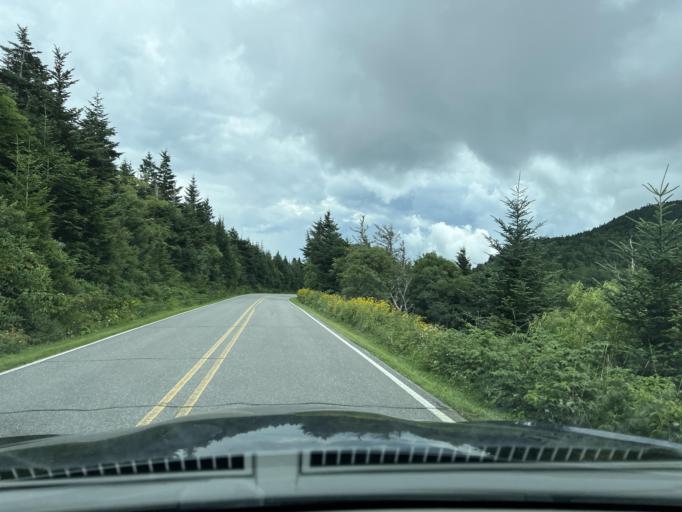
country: US
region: North Carolina
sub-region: Buncombe County
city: Black Mountain
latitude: 35.7476
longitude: -82.2776
